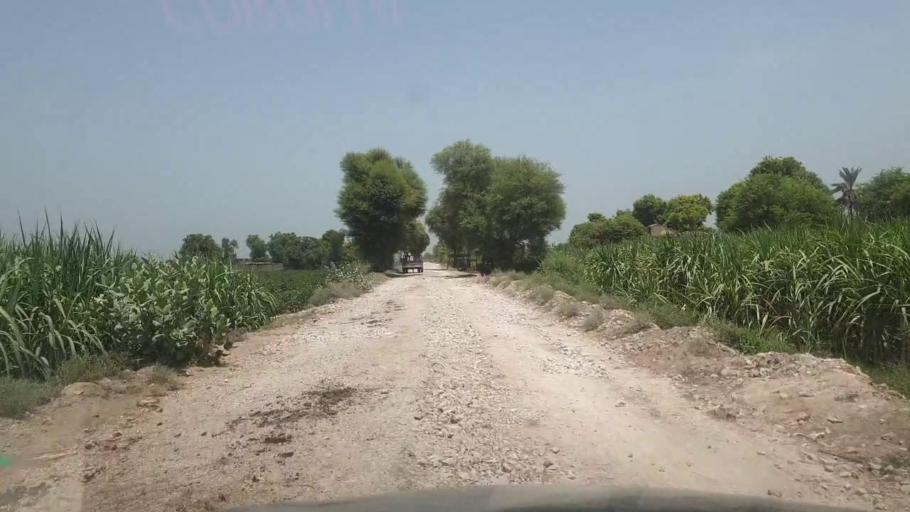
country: PK
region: Sindh
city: Sobhadero
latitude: 27.3285
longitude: 68.3551
